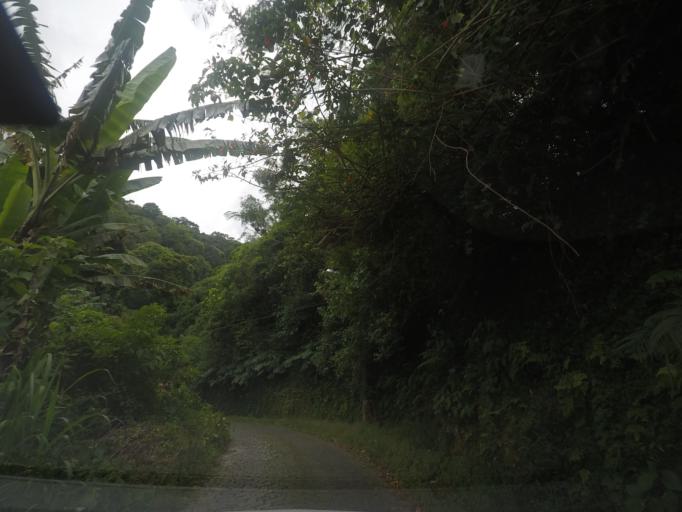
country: BR
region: Rio de Janeiro
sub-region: Petropolis
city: Petropolis
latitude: -22.4982
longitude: -43.1885
